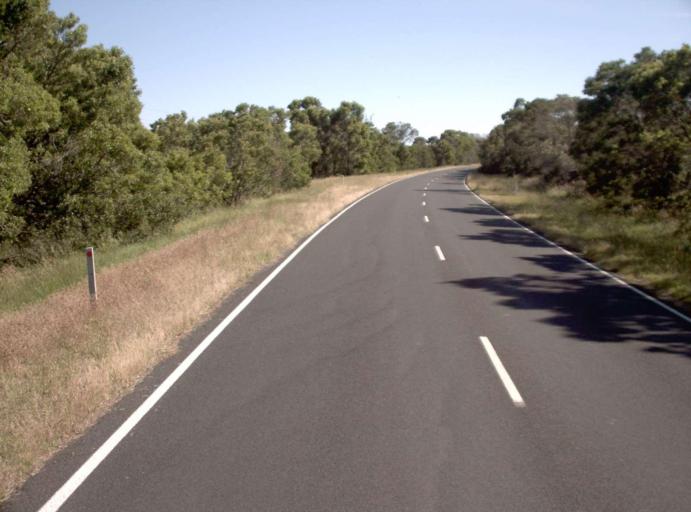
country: AU
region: Victoria
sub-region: Latrobe
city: Traralgon
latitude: -38.6330
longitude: 146.6758
